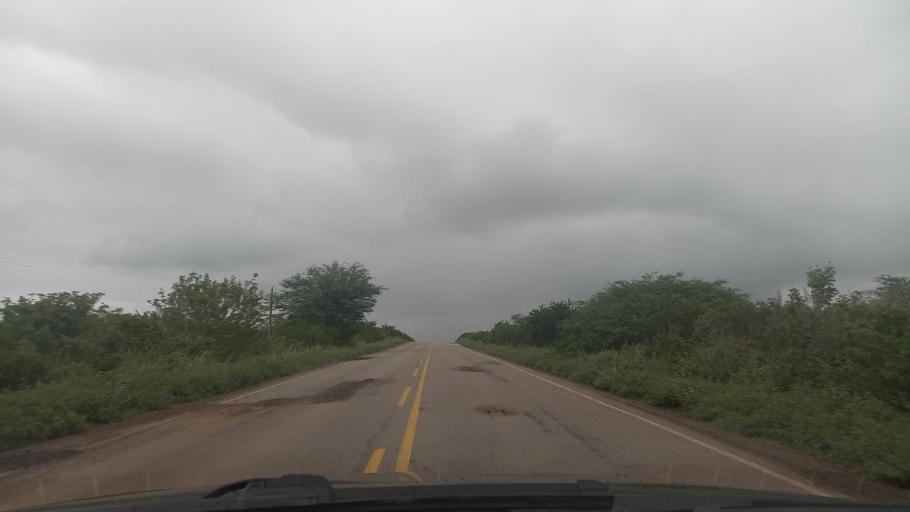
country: BR
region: Bahia
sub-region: Paulo Afonso
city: Paulo Afonso
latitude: -9.3281
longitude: -38.2874
